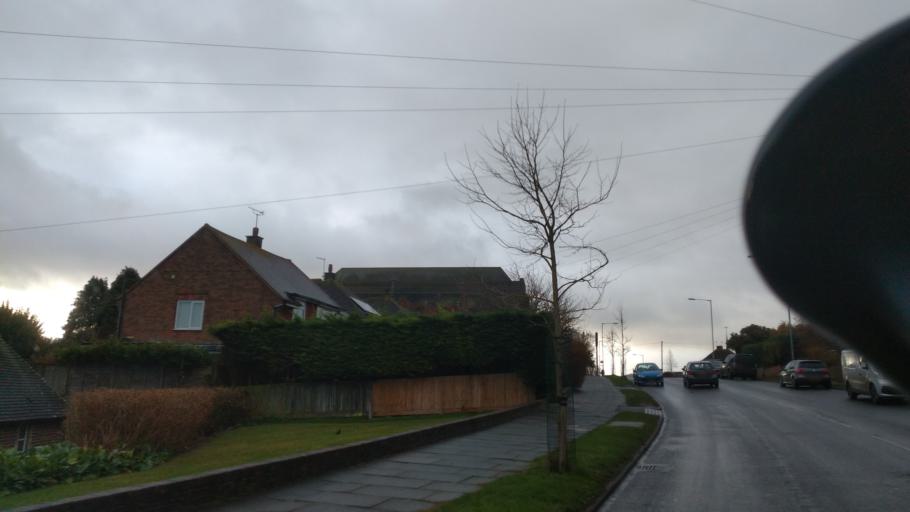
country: GB
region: England
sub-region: East Sussex
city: Eastbourne
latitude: 50.7843
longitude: 0.2542
